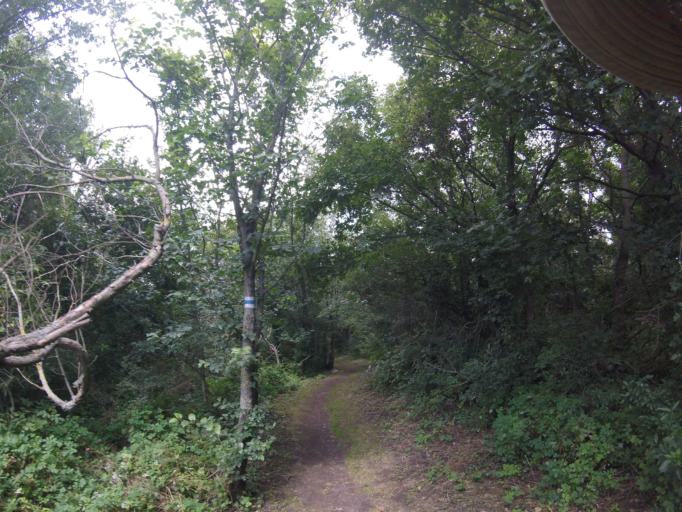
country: HU
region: Veszprem
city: Tapolca
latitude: 46.8428
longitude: 17.4502
